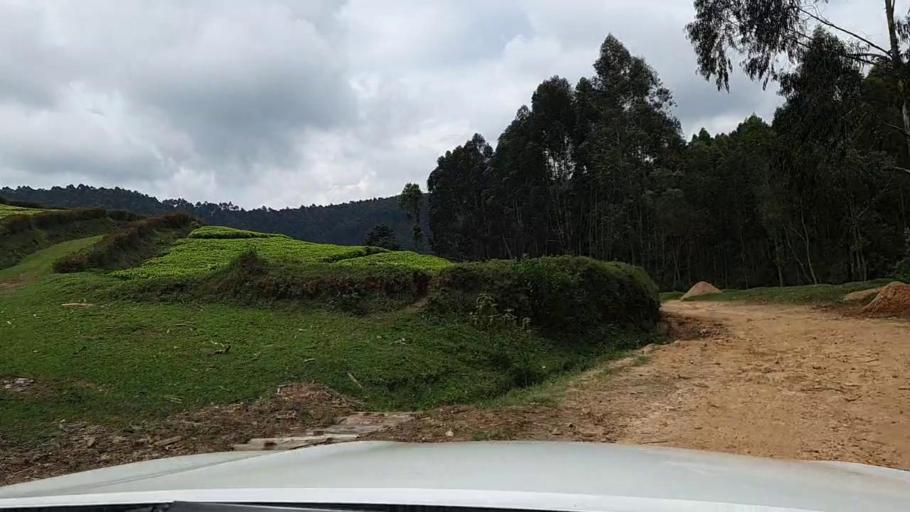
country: RW
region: Western Province
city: Kibuye
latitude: -2.2789
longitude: 29.3661
